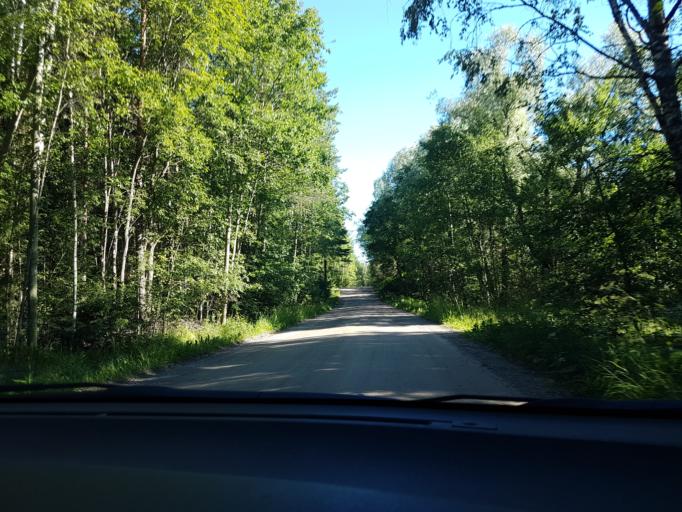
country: FI
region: Uusimaa
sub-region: Helsinki
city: Sibbo
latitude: 60.2735
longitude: 25.2342
